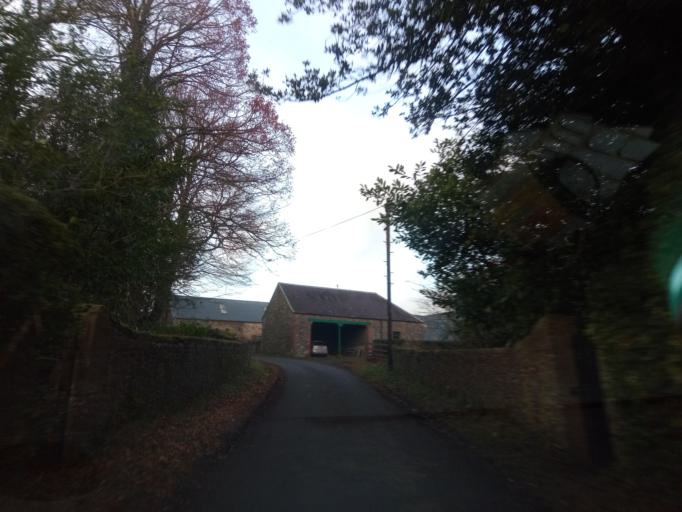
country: GB
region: Scotland
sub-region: The Scottish Borders
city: Newtown St Boswells
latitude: 55.5341
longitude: -2.7096
